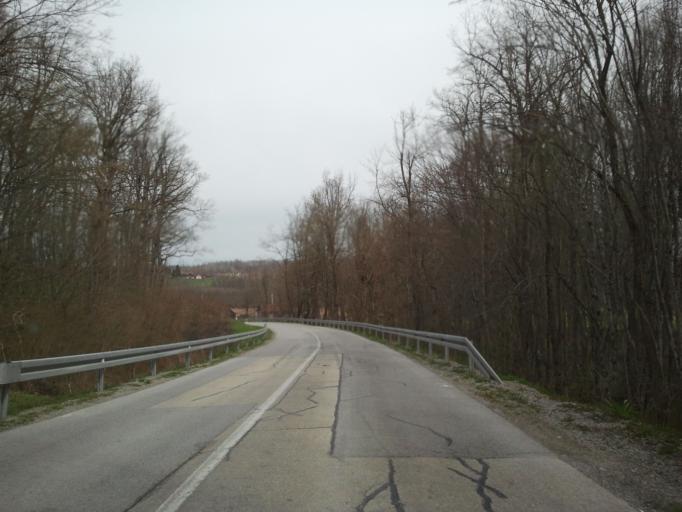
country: HR
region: Sisacko-Moslavacka
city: Gvozd
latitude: 45.3150
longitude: 15.9636
